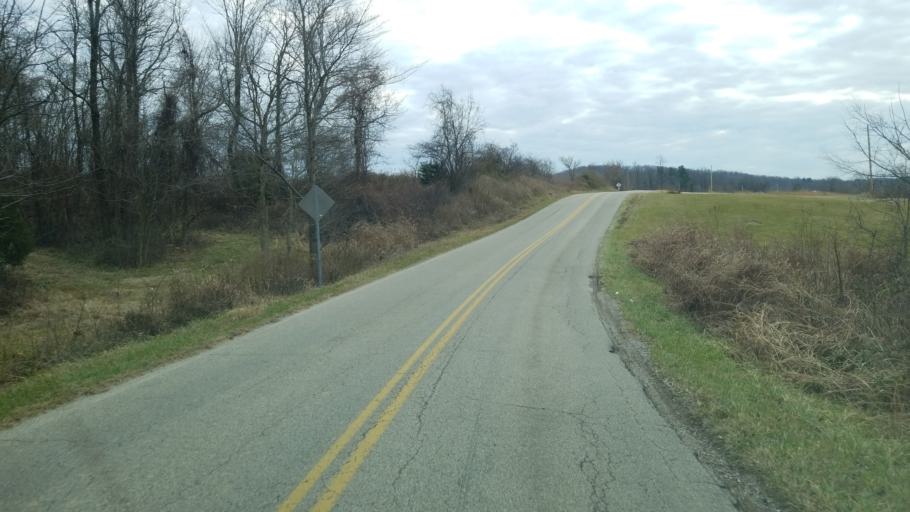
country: US
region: Ohio
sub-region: Highland County
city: Greenfield
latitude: 39.2926
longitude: -83.3633
